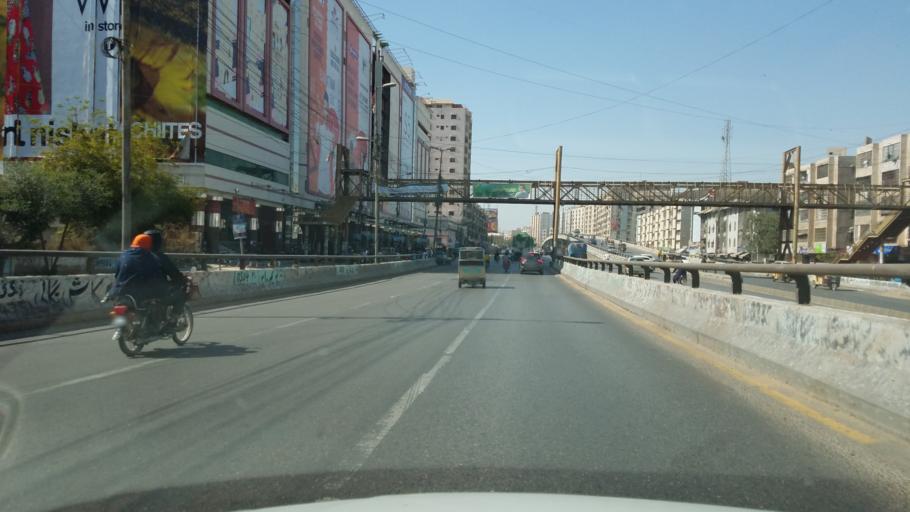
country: PK
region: Sindh
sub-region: Karachi District
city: Karachi
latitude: 24.9022
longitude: 67.1153
